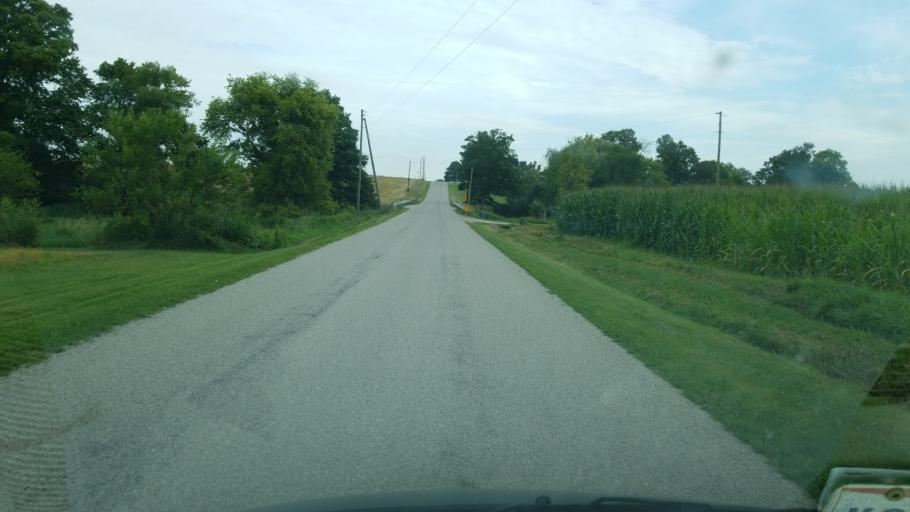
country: US
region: Ohio
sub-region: Seneca County
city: Tiffin
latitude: 41.0350
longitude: -83.0545
